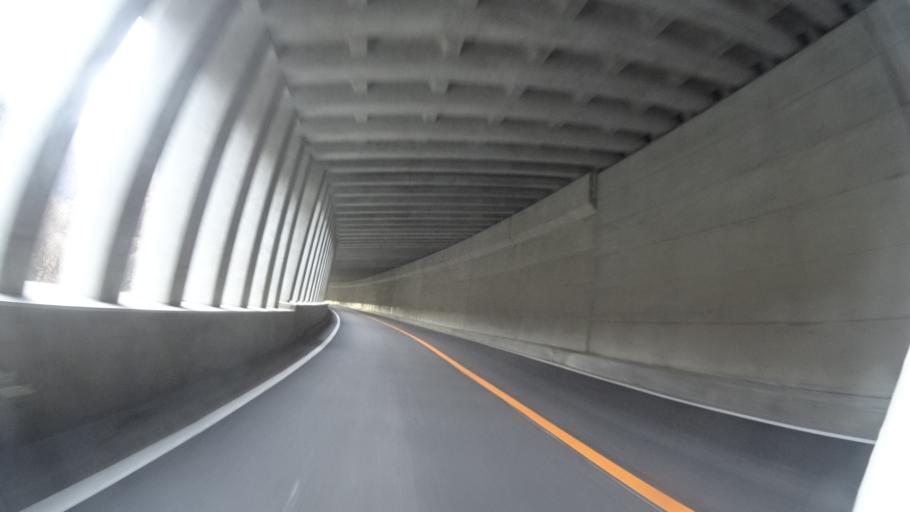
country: JP
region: Fukui
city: Ono
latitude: 35.9272
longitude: 136.6392
